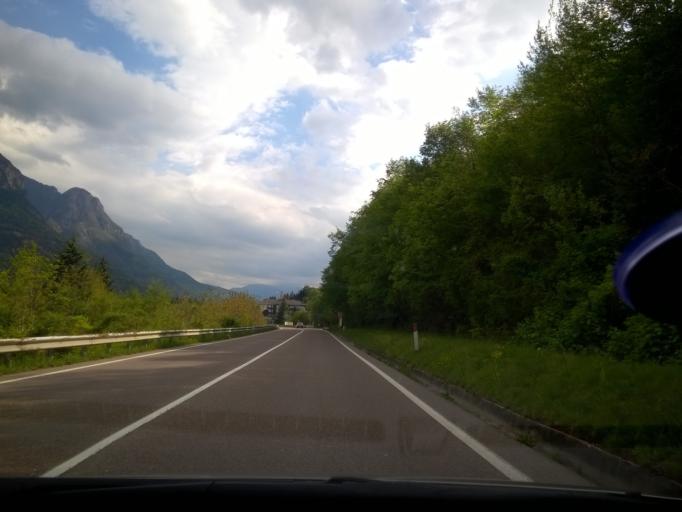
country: IT
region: Veneto
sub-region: Provincia di Belluno
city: Longarone
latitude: 46.2512
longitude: 12.2983
